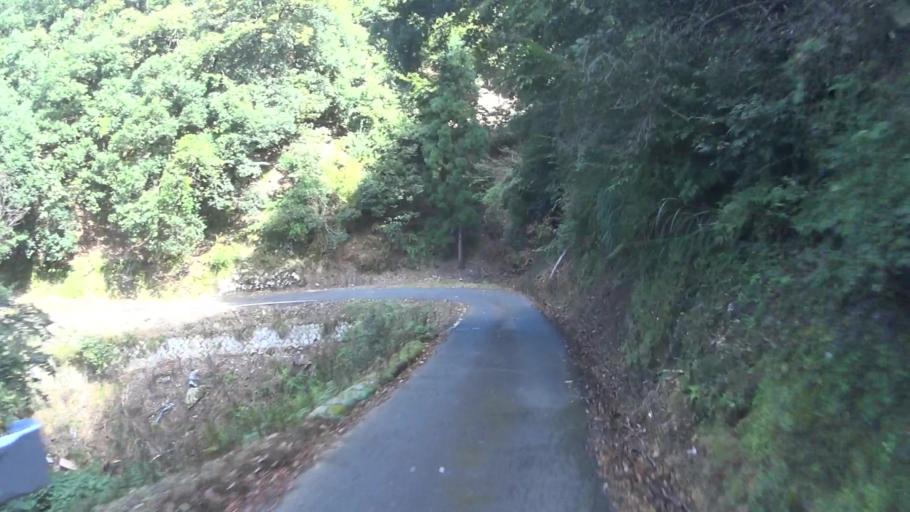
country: JP
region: Hyogo
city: Toyooka
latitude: 35.6098
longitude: 134.9950
